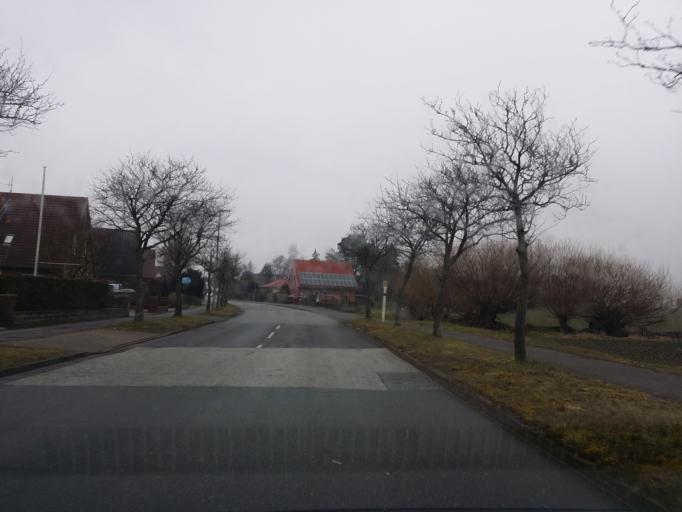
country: DE
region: Schleswig-Holstein
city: Burg auf Fehmarn
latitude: 54.4200
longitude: 11.2097
